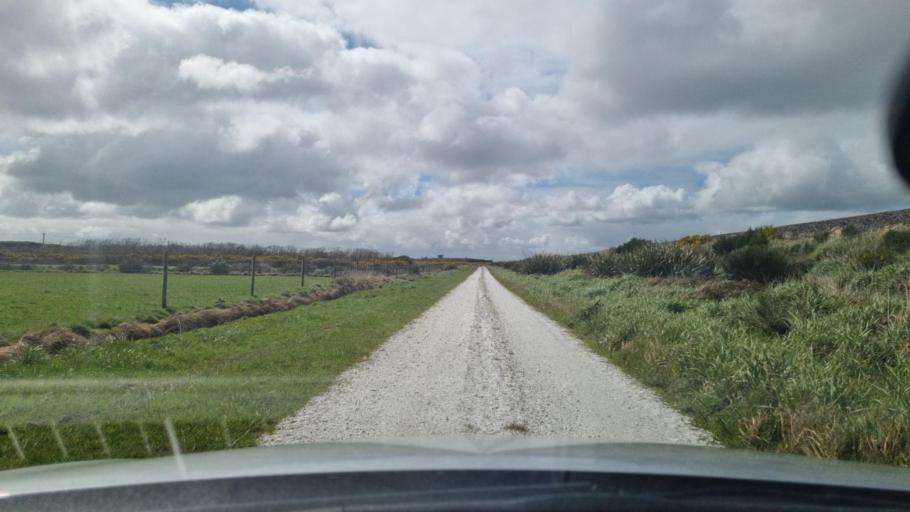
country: NZ
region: Southland
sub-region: Invercargill City
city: Bluff
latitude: -46.5333
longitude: 168.3046
